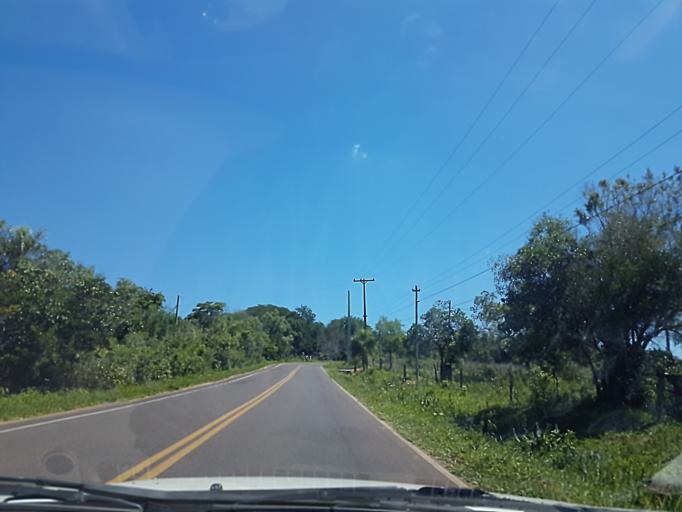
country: PY
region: Cordillera
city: Altos
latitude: -25.2439
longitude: -57.2326
